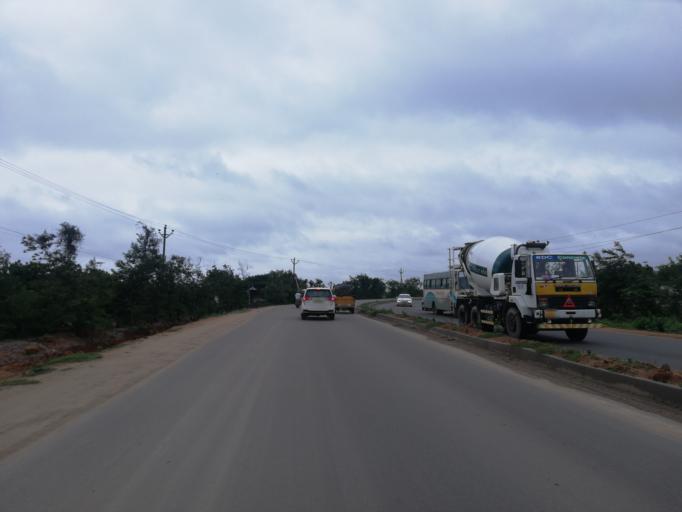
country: IN
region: Telangana
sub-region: Rangareddi
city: Quthbullapur
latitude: 17.5667
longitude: 78.4191
